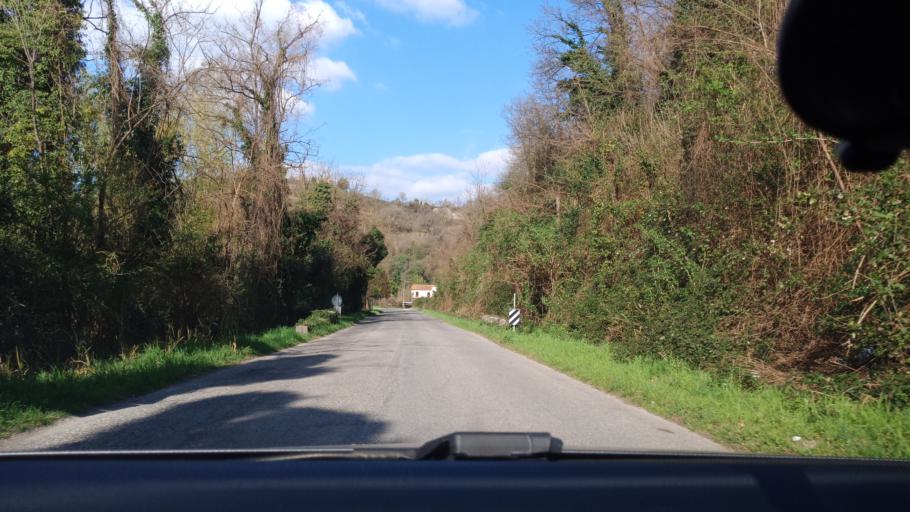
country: IT
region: Latium
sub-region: Citta metropolitana di Roma Capitale
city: Torrita Tiberina
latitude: 42.2369
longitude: 12.6329
